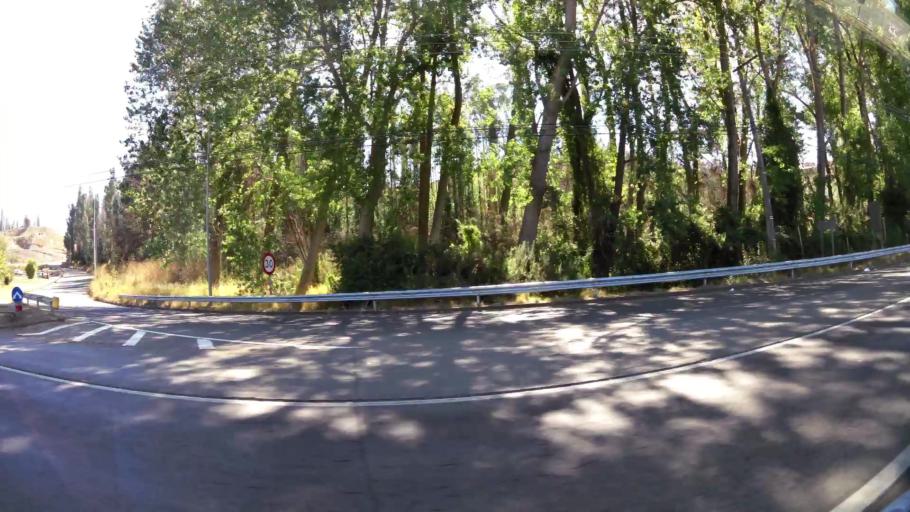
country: CL
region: Biobio
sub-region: Provincia de Concepcion
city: Penco
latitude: -36.7531
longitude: -73.0006
